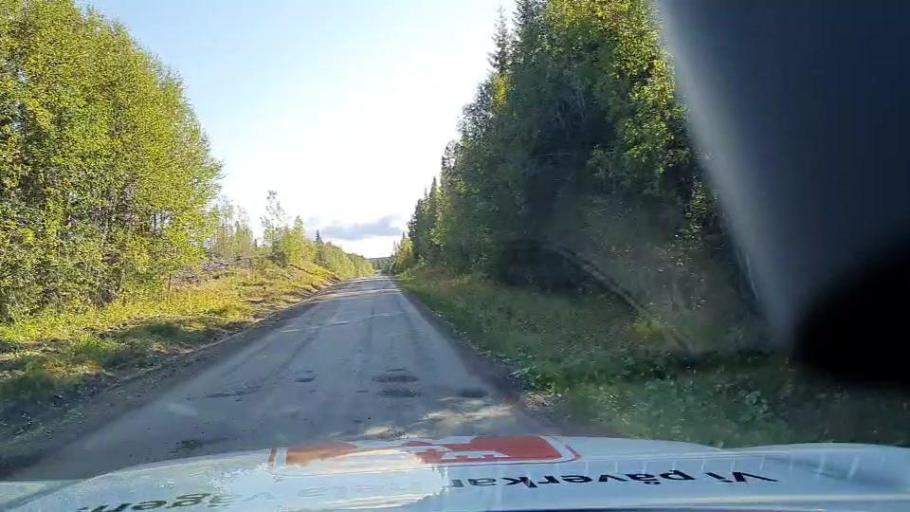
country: SE
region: Jaemtland
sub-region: Stroemsunds Kommun
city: Stroemsund
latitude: 64.5556
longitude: 15.0926
